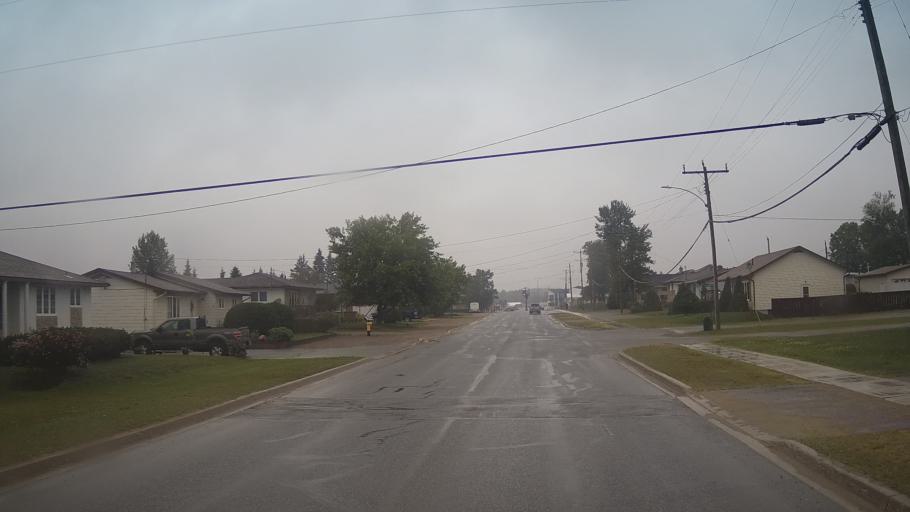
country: CA
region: Ontario
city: Greenstone
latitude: 49.7773
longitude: -86.5356
